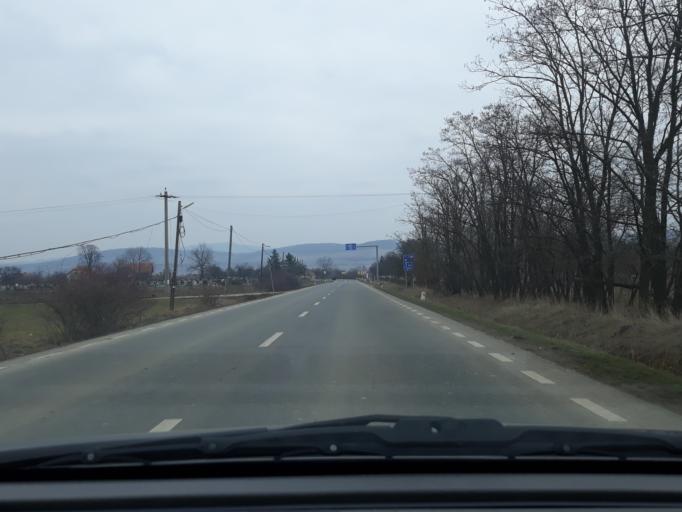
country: RO
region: Salaj
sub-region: Comuna Nusfalau
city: Nusfalau
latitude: 47.1878
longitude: 22.6978
